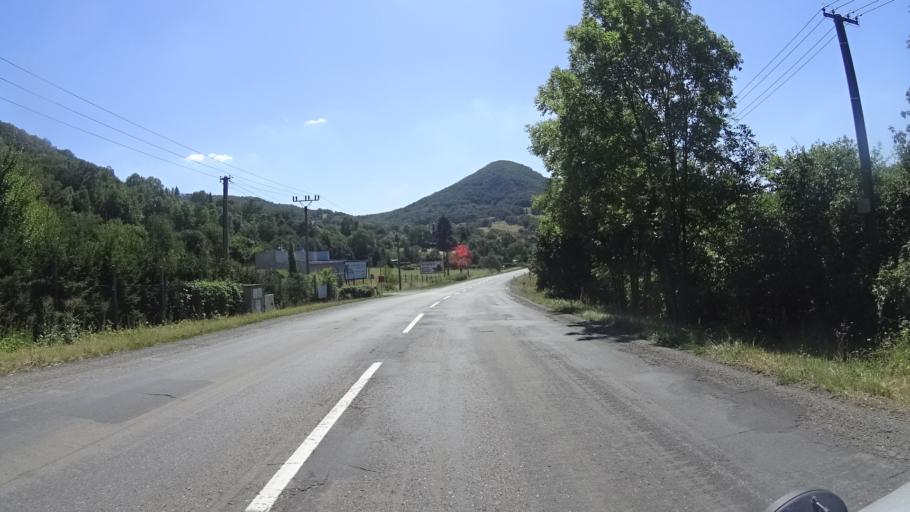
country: CZ
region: Ustecky
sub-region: Okres Usti nad Labem
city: Usti nad Labem
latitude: 50.5982
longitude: 14.0725
